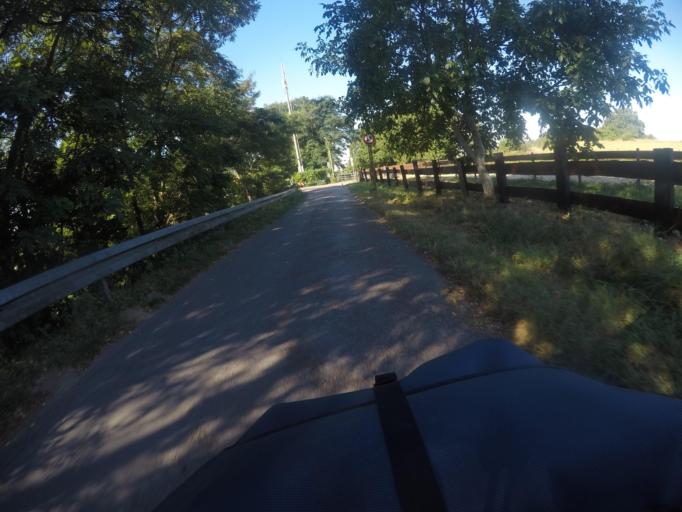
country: DE
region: North Rhine-Westphalia
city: Haan
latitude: 51.1705
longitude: 6.9976
